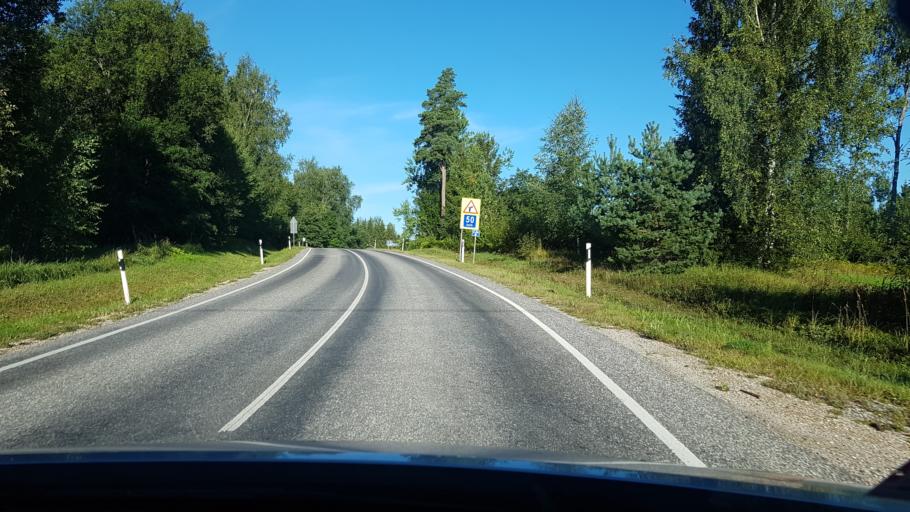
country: EE
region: Vorumaa
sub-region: Antsla vald
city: Vana-Antsla
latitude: 58.0216
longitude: 26.5849
